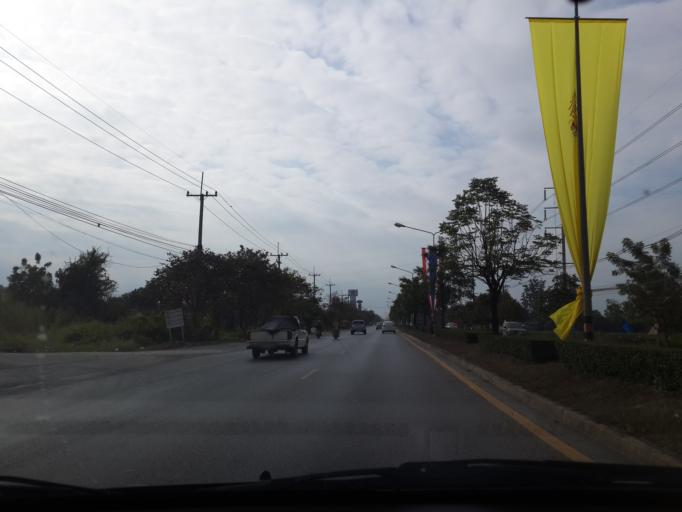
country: TH
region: Chiang Mai
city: San Sai
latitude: 18.8611
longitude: 99.0148
